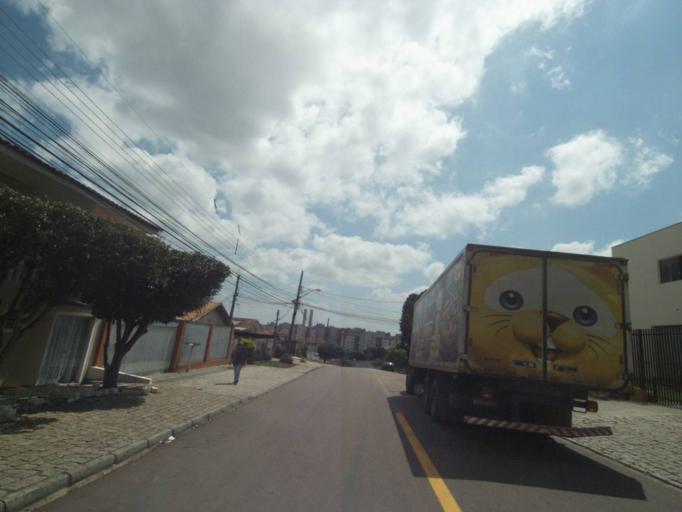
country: BR
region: Parana
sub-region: Curitiba
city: Curitiba
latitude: -25.5025
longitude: -49.3048
